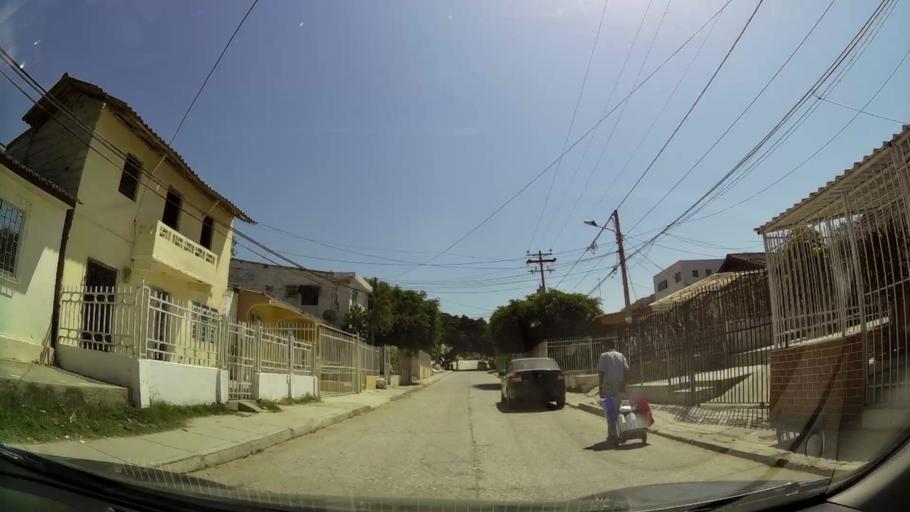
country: CO
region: Bolivar
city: Cartagena
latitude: 10.4306
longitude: -75.5316
